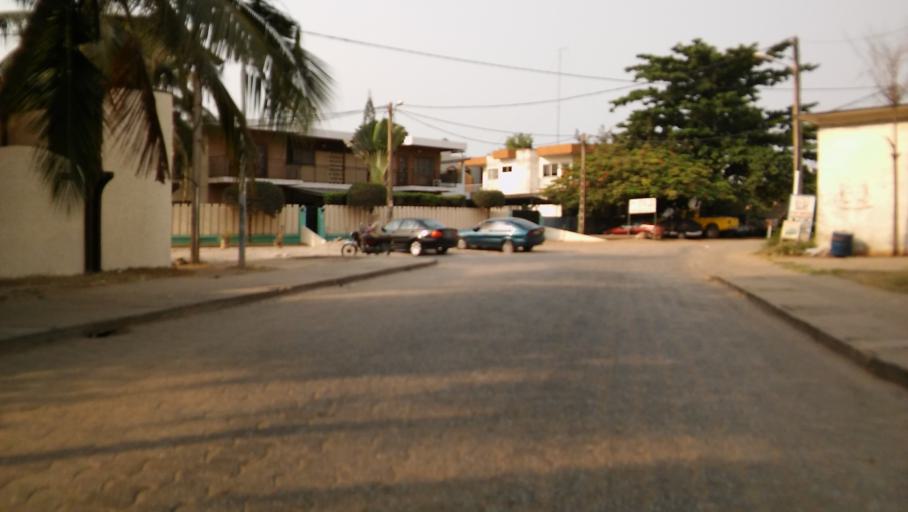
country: BJ
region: Littoral
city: Cotonou
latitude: 6.3551
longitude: 2.3983
